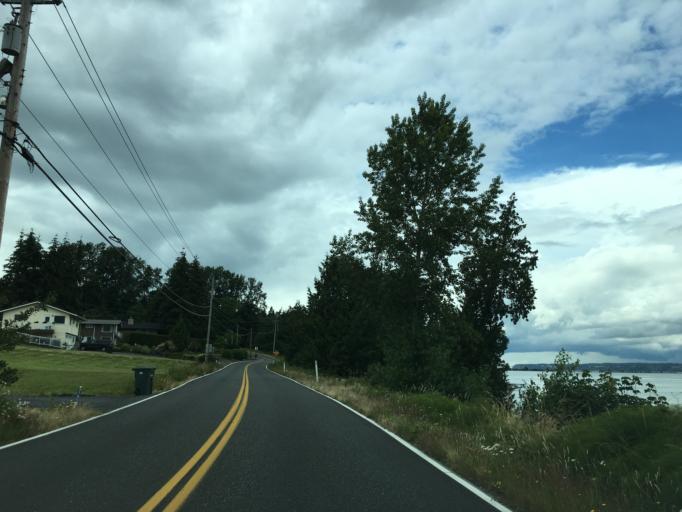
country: US
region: Washington
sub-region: Whatcom County
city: Blaine
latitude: 48.9615
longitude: -122.7619
